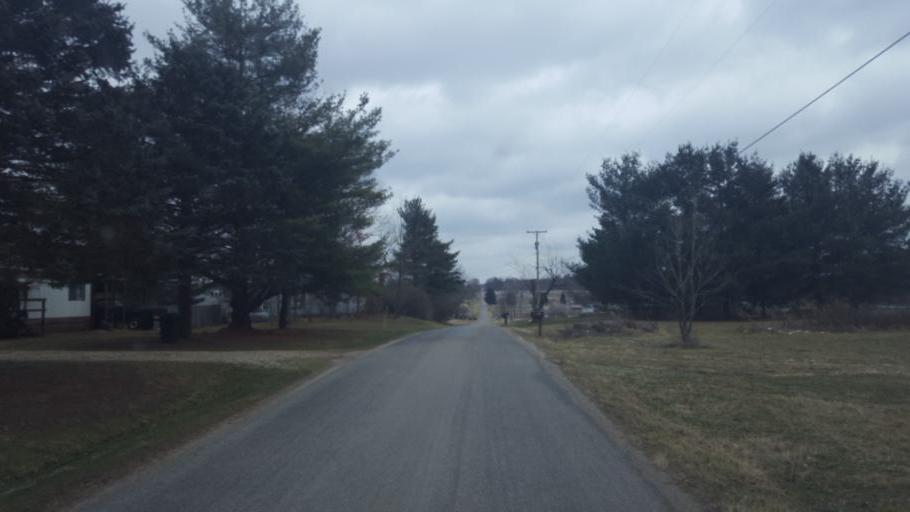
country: US
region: Ohio
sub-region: Crawford County
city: Crestline
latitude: 40.7183
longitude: -82.7061
